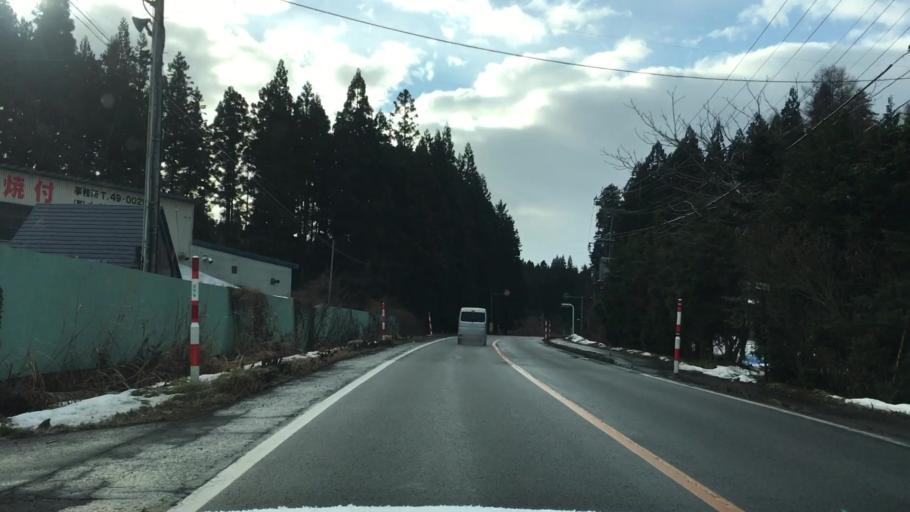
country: JP
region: Akita
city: Odate
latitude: 40.3278
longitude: 140.5828
